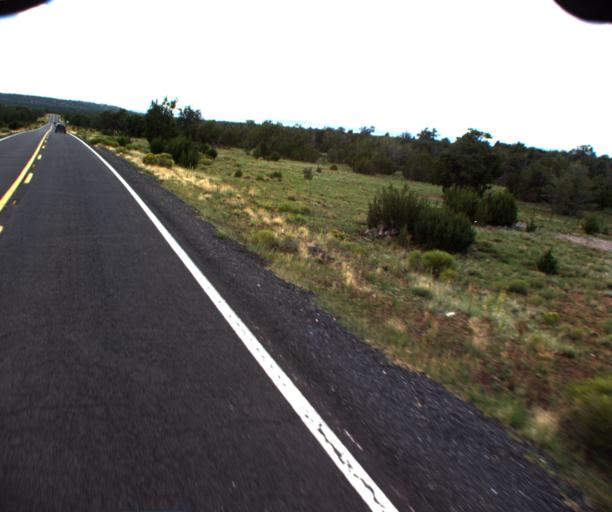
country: US
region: Arizona
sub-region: Coconino County
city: Parks
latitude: 35.5268
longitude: -111.8422
